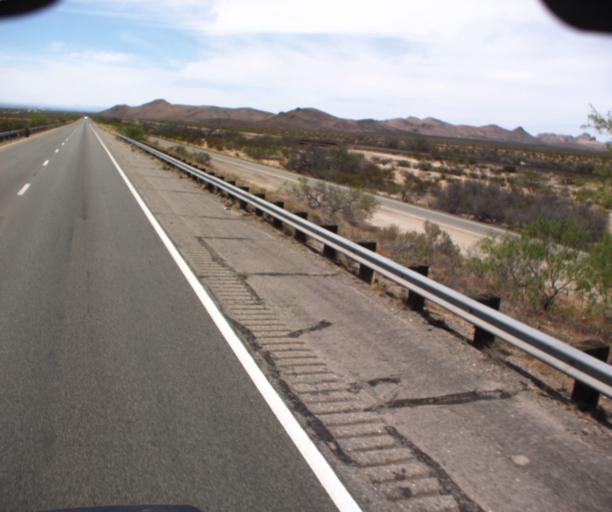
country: US
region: New Mexico
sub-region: Hidalgo County
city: Lordsburg
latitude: 32.2298
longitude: -109.0559
